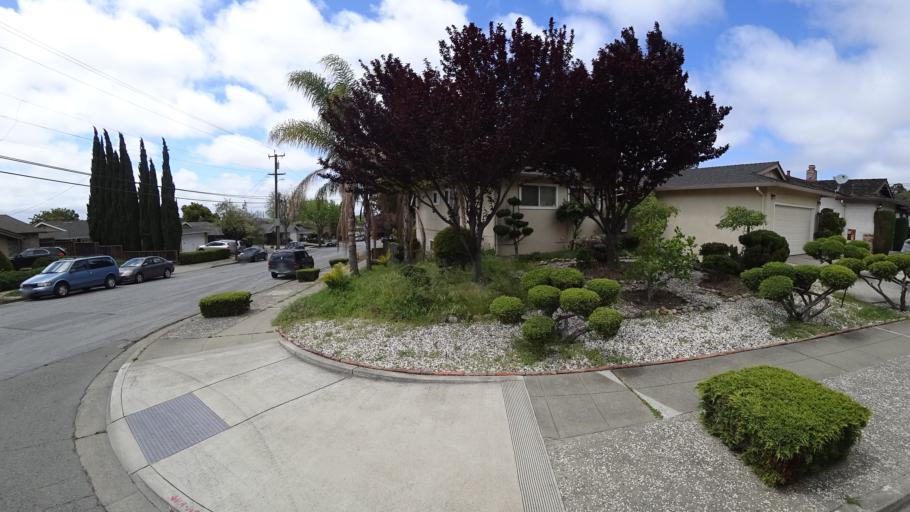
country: US
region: California
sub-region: Alameda County
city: Union City
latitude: 37.6305
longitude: -122.0428
